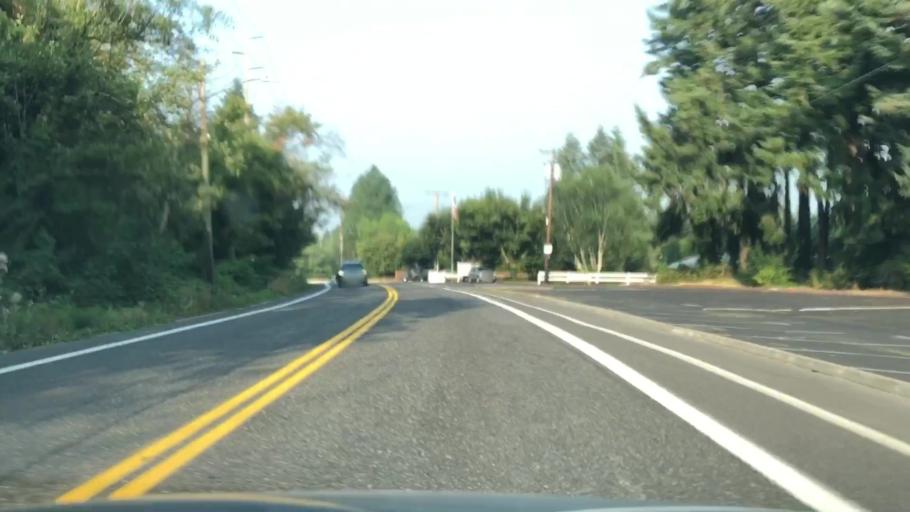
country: US
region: Oregon
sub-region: Washington County
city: Garden Home-Whitford
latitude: 45.4681
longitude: -122.7261
